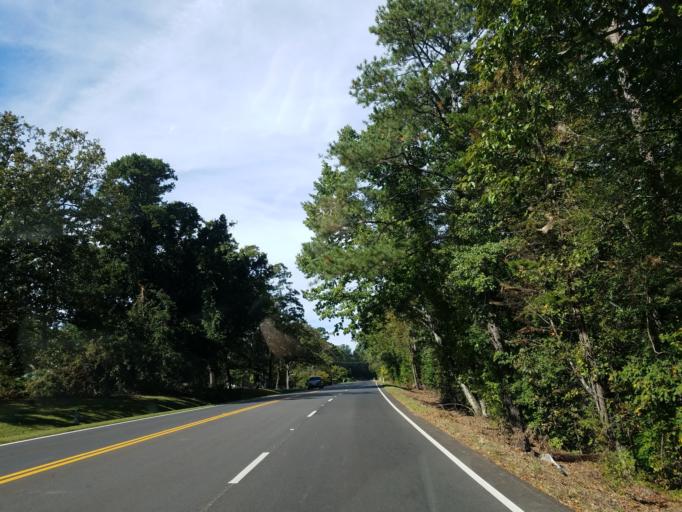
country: US
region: Georgia
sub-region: Pickens County
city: Nelson
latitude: 34.4252
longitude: -84.3957
